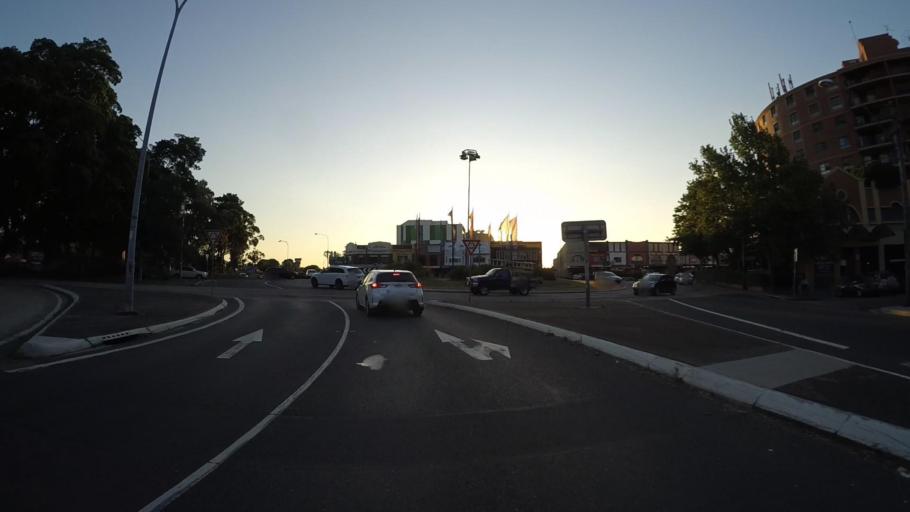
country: AU
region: New South Wales
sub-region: Randwick
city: Kingsford
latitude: -33.9243
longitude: 151.2288
